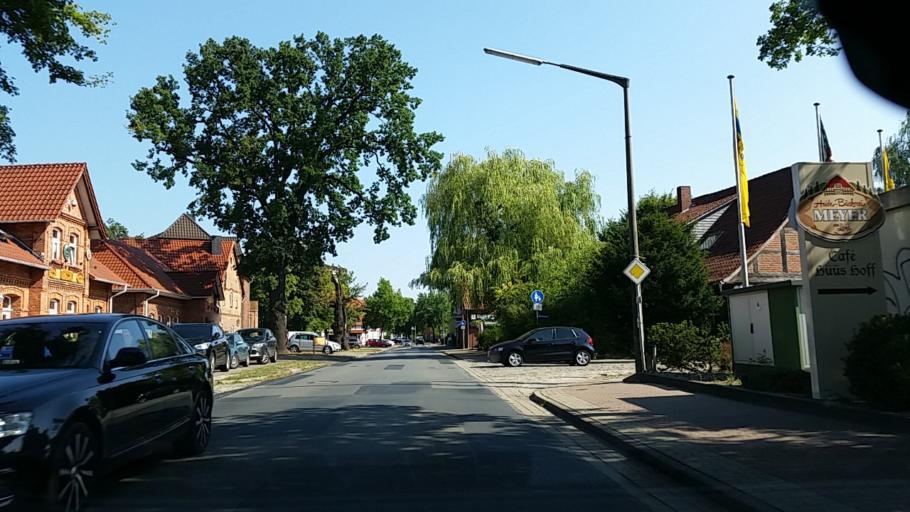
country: DE
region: Lower Saxony
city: Wahrenholz
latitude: 52.6137
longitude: 10.6020
